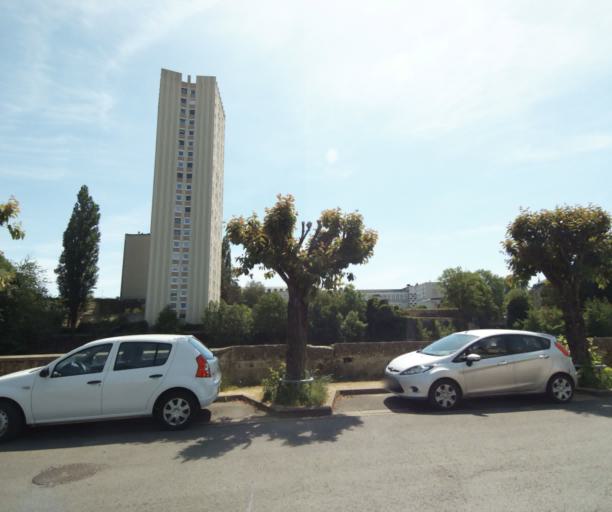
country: FR
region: Champagne-Ardenne
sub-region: Departement des Ardennes
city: Charleville-Mezieres
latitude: 49.7627
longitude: 4.7223
